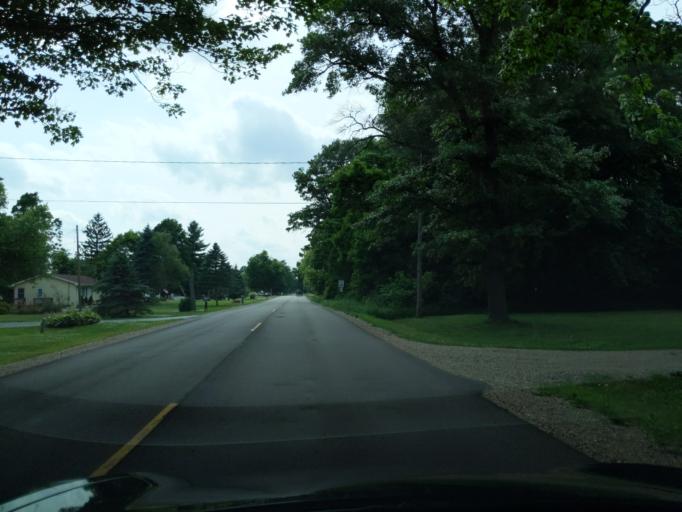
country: US
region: Michigan
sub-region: Eaton County
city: Eaton Rapids
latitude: 42.5094
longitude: -84.6206
